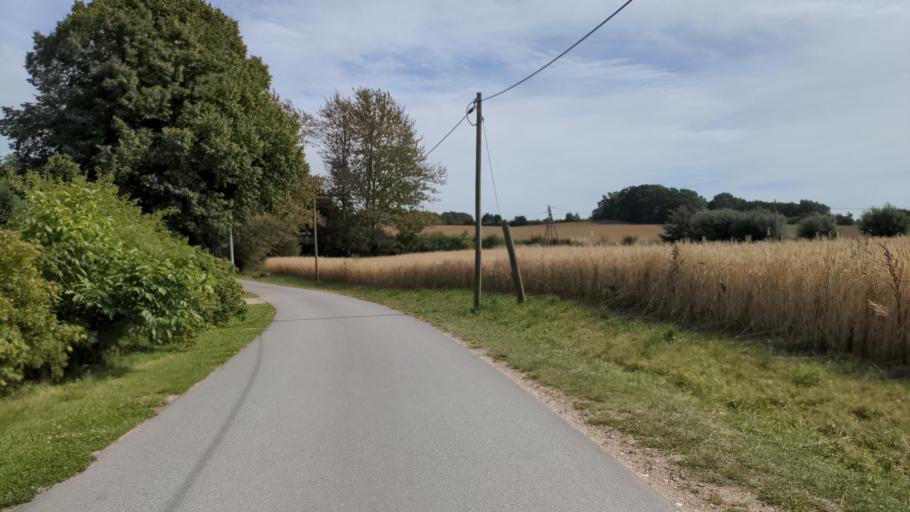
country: DE
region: Mecklenburg-Vorpommern
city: Kalkhorst
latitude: 54.0012
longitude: 11.0739
